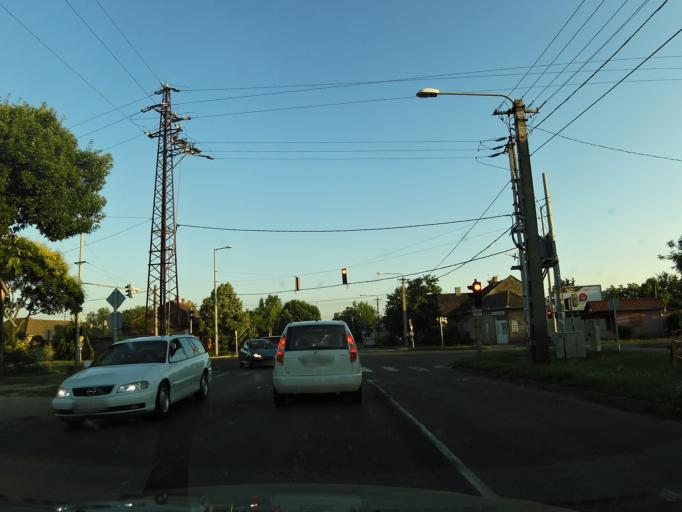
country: HU
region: Csongrad
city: Hodmezovasarhely
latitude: 46.4308
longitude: 20.3189
